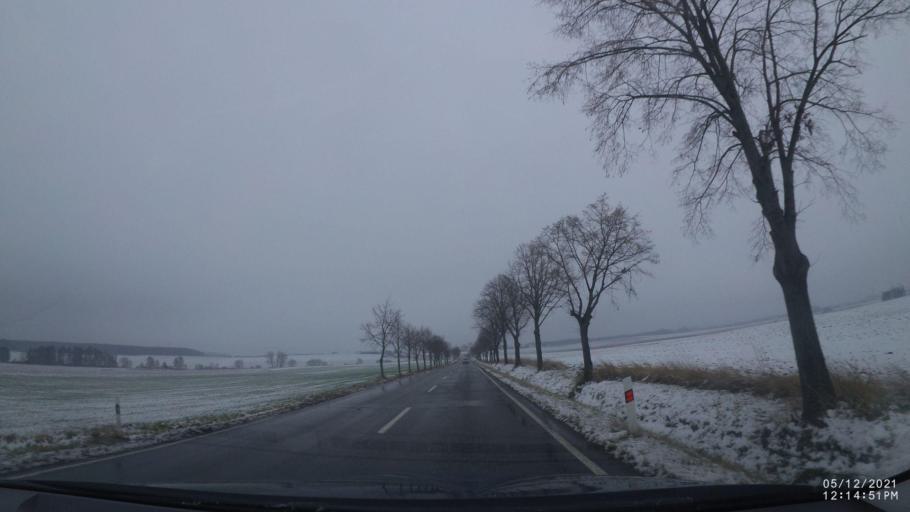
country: CZ
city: Ceske Mezirici
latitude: 50.3057
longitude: 16.0370
